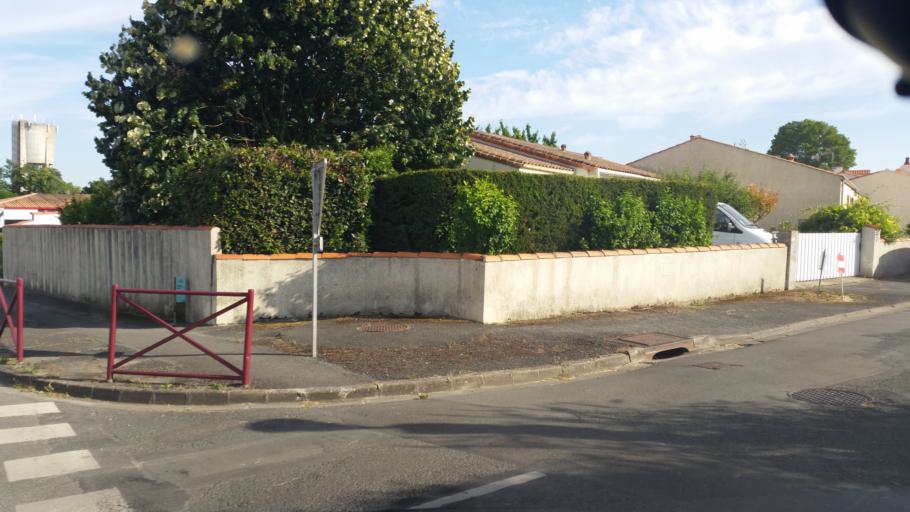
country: FR
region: Poitou-Charentes
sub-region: Departement de la Charente-Maritime
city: Marans
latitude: 46.3041
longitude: -0.9868
